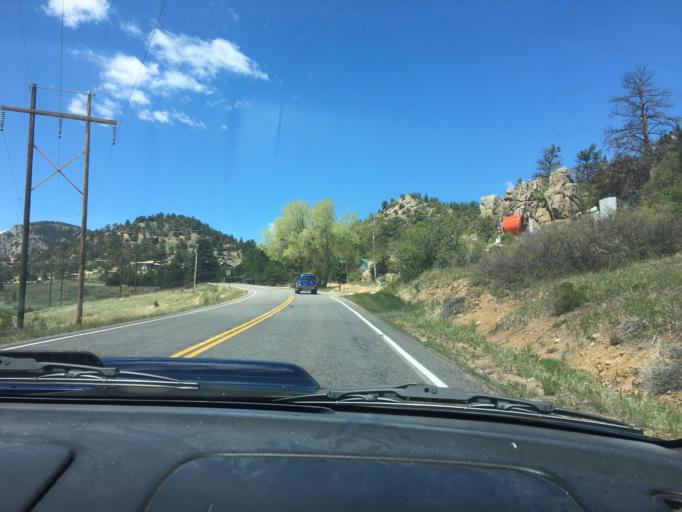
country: US
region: Colorado
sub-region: Larimer County
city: Estes Park
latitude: 40.3532
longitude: -105.5225
